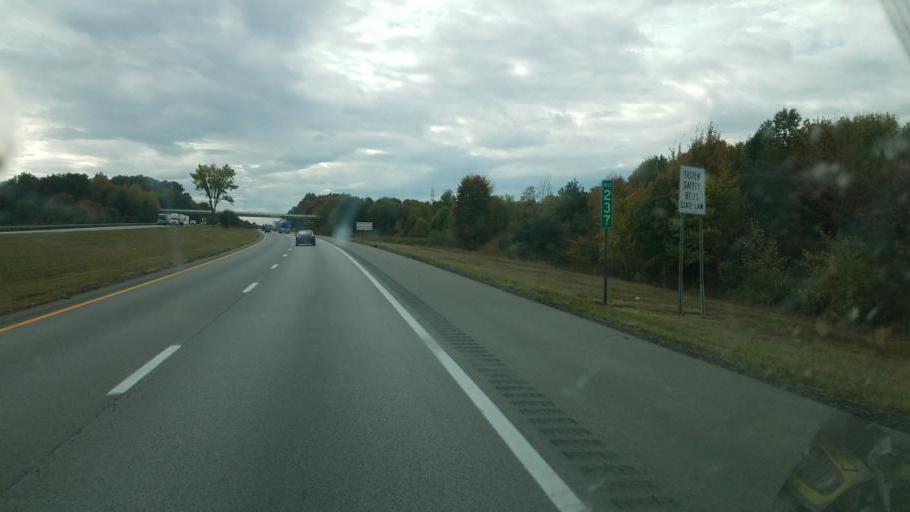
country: US
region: Ohio
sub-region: Trumbull County
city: Masury
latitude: 41.1828
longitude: -80.5231
